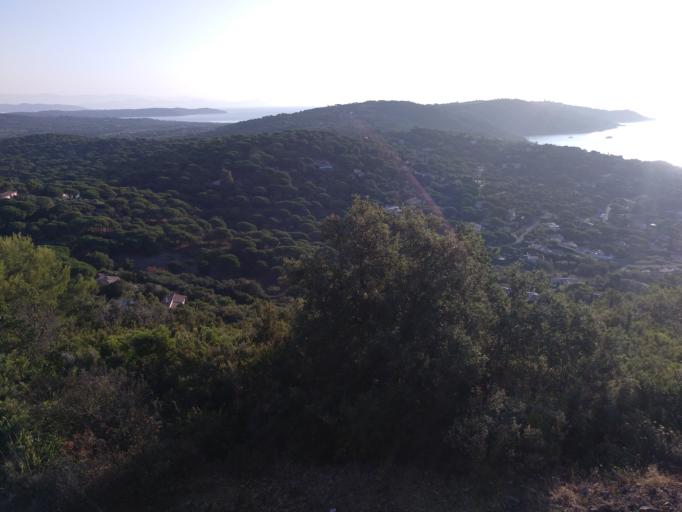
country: FR
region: Provence-Alpes-Cote d'Azur
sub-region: Departement du Var
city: Ramatuelle
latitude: 43.1864
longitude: 6.6356
